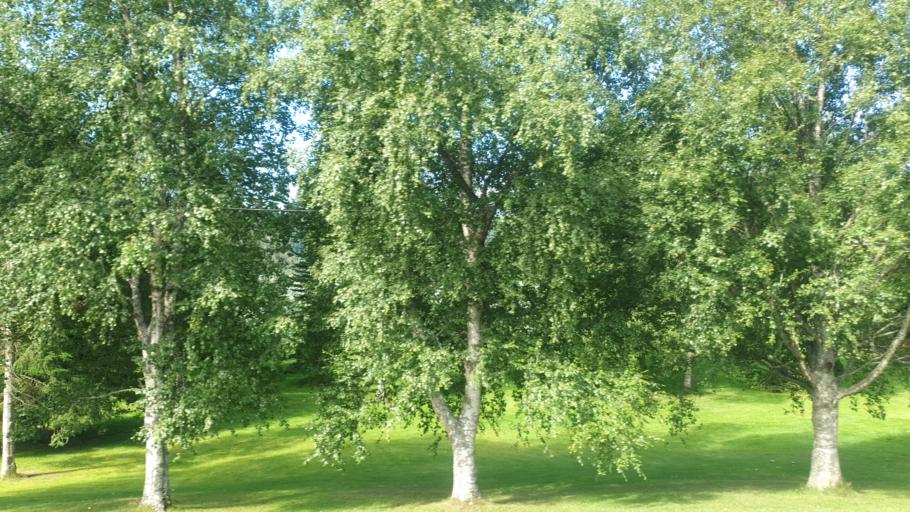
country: NO
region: Sor-Trondelag
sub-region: Orkdal
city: Orkanger
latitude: 63.2722
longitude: 9.8205
